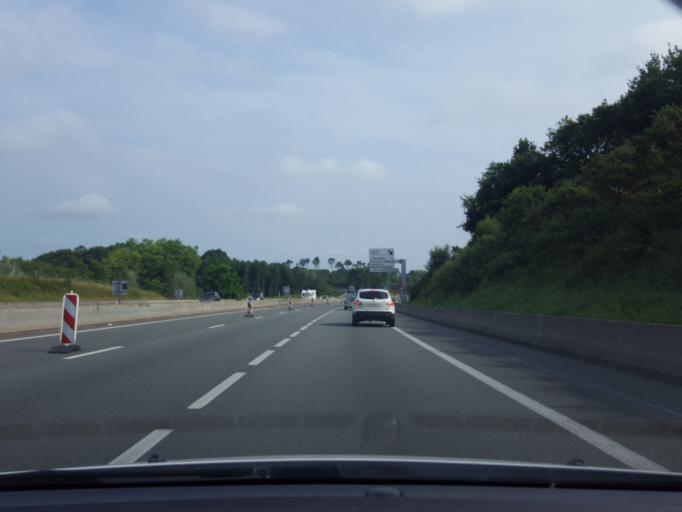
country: FR
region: Aquitaine
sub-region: Departement des Landes
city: Ondres
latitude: 43.5369
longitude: -1.4315
